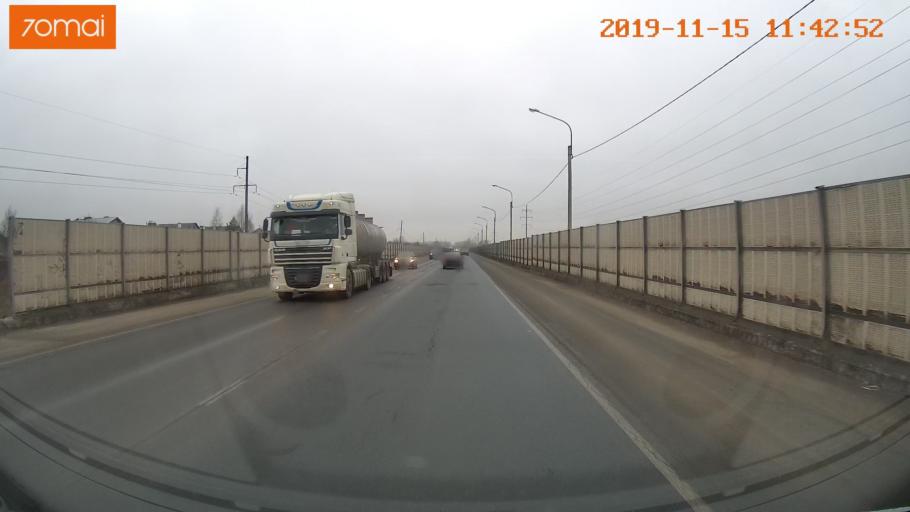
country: RU
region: Vologda
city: Vologda
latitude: 59.2230
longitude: 39.7747
